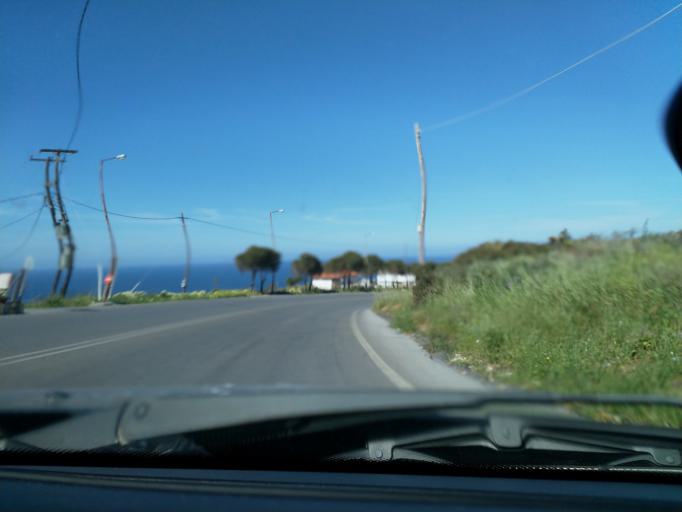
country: GR
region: Crete
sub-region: Nomos Rethymnis
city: Rethymno
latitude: 35.3546
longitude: 24.4612
